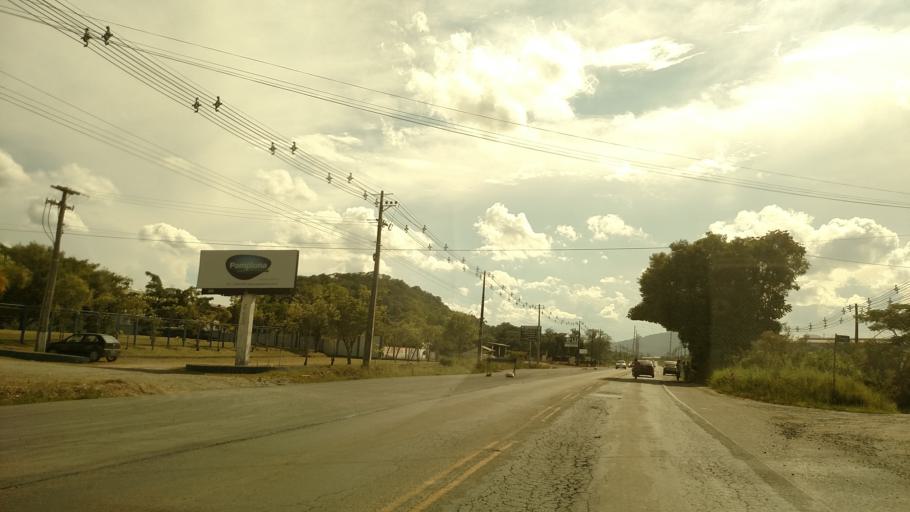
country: BR
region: Santa Catarina
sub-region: Itajai
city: Itajai
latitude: -26.9458
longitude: -48.7206
